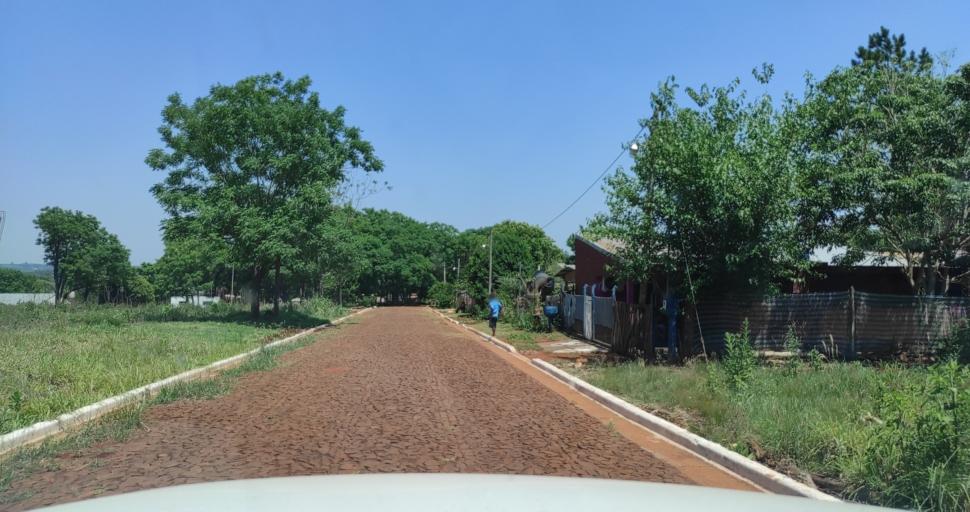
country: AR
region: Misiones
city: Santo Pipo
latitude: -27.1081
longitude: -55.3420
